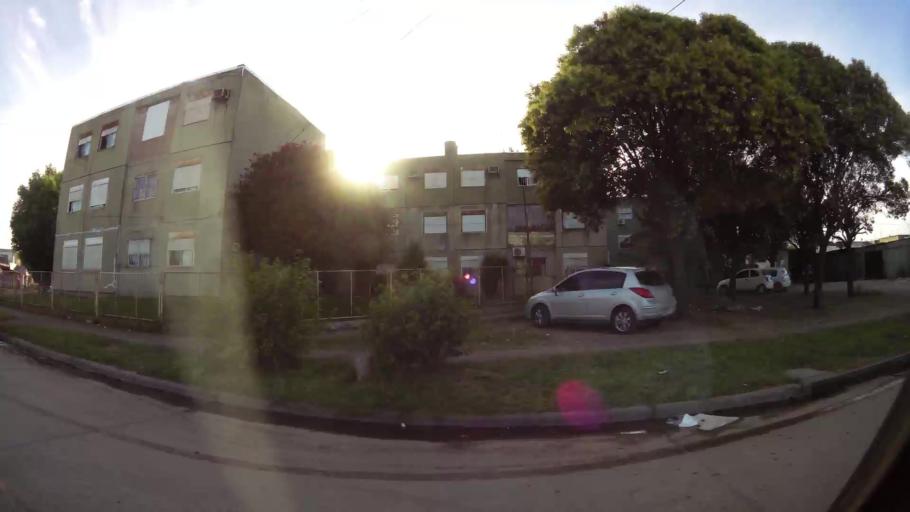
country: AR
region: Buenos Aires
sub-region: Partido de Almirante Brown
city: Adrogue
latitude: -34.8212
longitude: -58.3418
